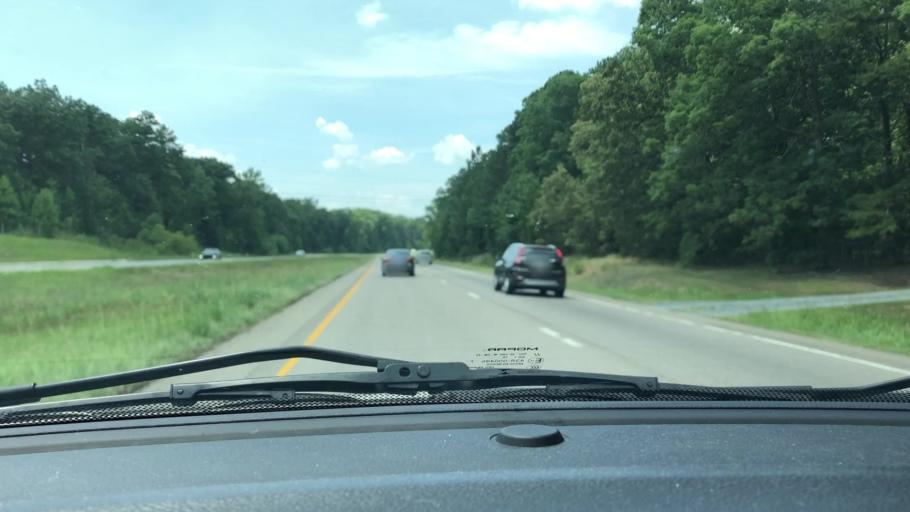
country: US
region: North Carolina
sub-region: Chatham County
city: Farmville
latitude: 35.5699
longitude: -79.3033
